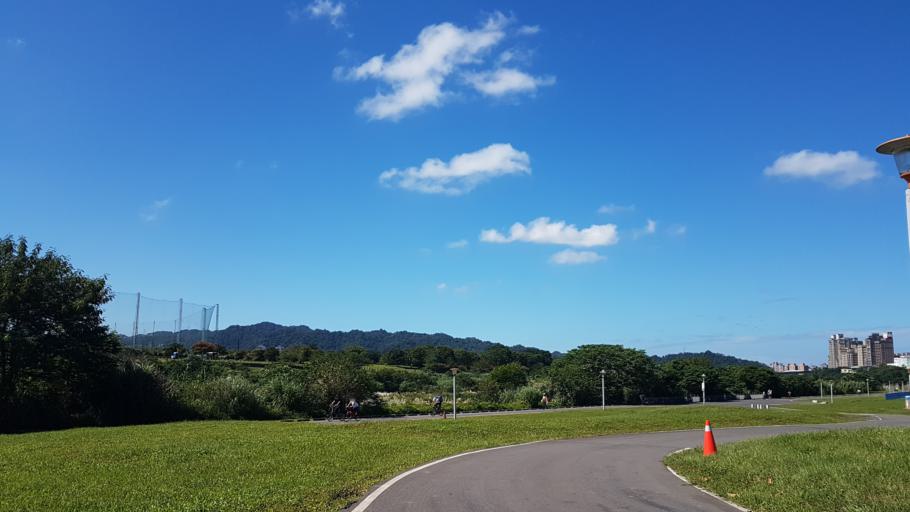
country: TW
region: Taipei
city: Taipei
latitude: 24.9648
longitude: 121.5356
